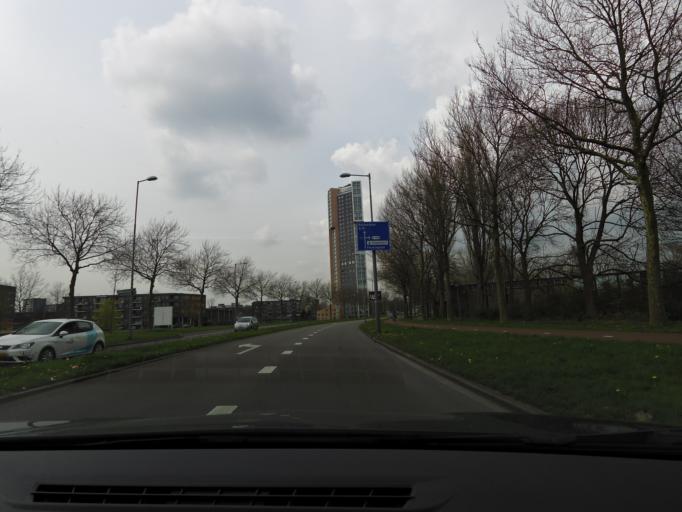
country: NL
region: South Holland
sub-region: Gemeente Spijkenisse
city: Spijkenisse
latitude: 51.8605
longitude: 4.3549
